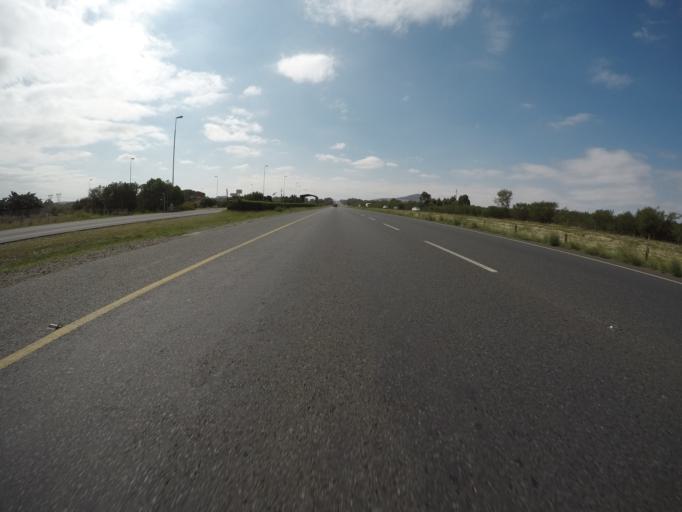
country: ZA
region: Western Cape
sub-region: City of Cape Town
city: Sunset Beach
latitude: -33.7608
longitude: 18.5471
